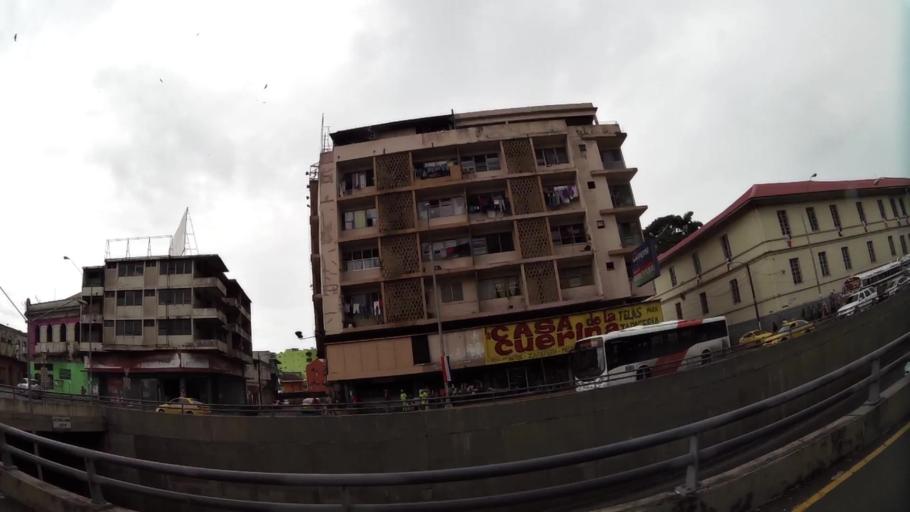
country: PA
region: Panama
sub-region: Distrito de Panama
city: Ancon
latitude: 8.9589
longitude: -79.5433
